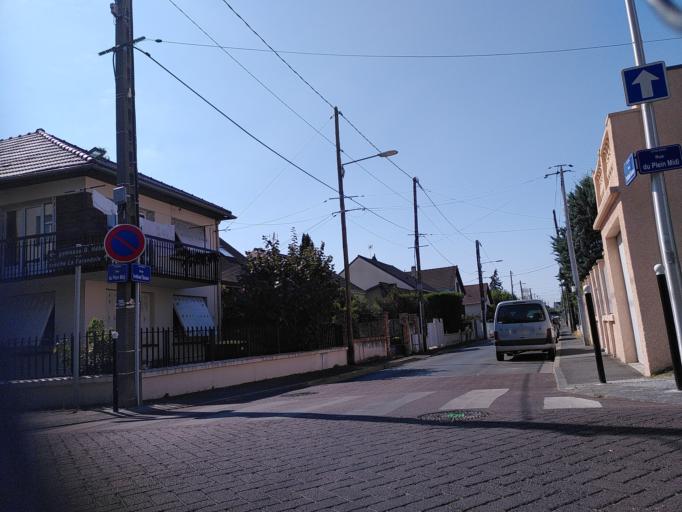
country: FR
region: Ile-de-France
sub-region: Departement de l'Essonne
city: Paray-Vieille-Poste
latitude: 48.7020
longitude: 2.3623
